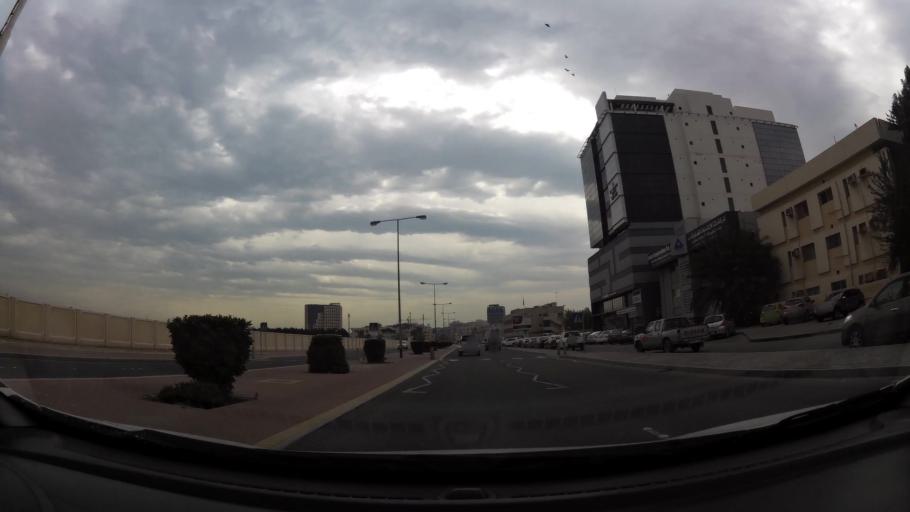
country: BH
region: Manama
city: Manama
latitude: 26.2100
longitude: 50.5932
